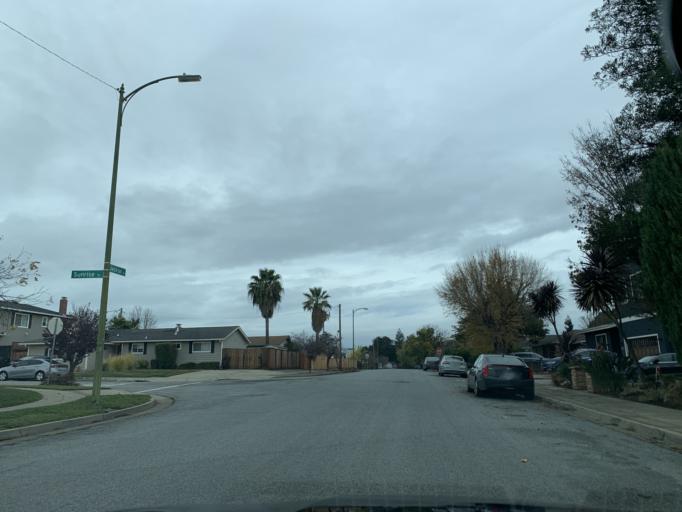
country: US
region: California
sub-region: Santa Clara County
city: Cambrian Park
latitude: 37.2580
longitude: -121.9404
